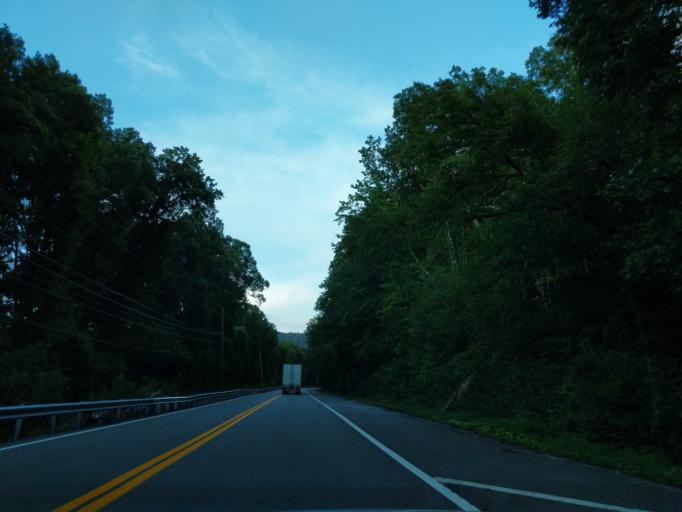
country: US
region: Tennessee
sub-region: Hamilton County
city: Lookout Mountain
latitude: 35.0313
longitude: -85.4304
